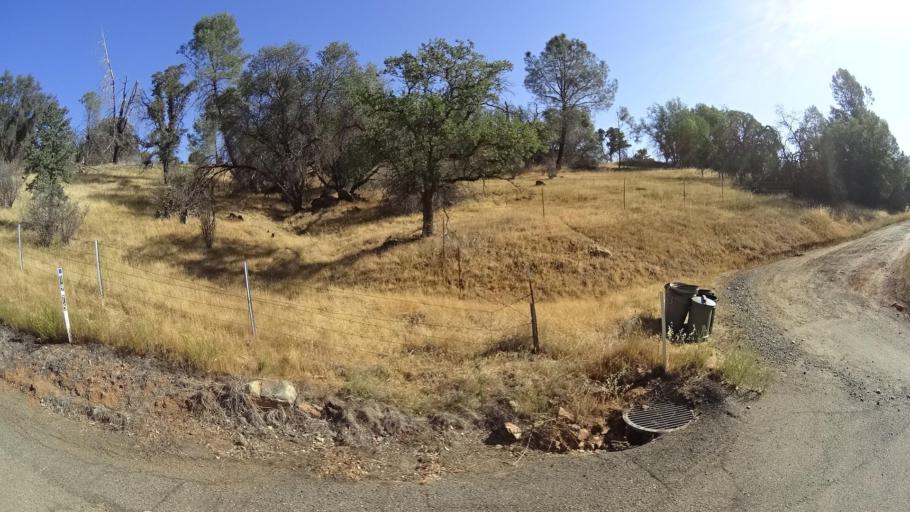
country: US
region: California
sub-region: Mariposa County
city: Mariposa
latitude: 37.5667
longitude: -120.1308
